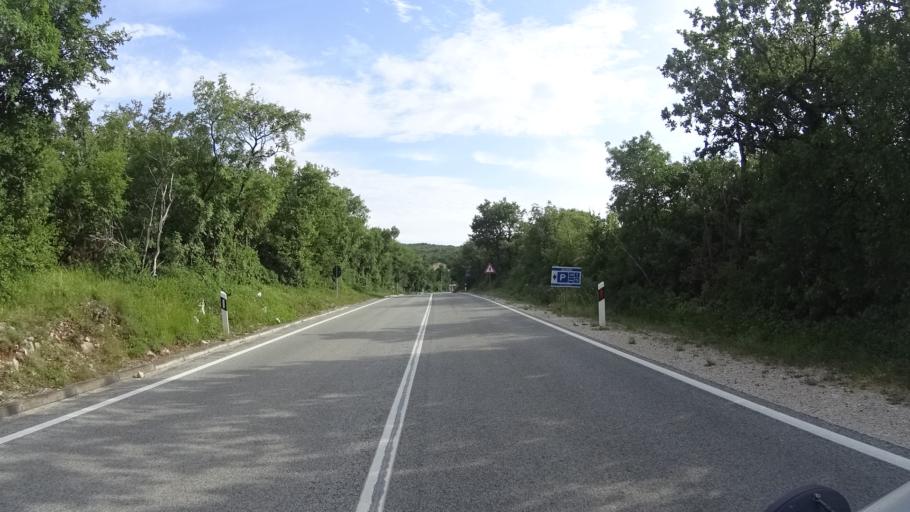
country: HR
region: Istarska
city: Rasa
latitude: 45.0570
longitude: 14.0895
